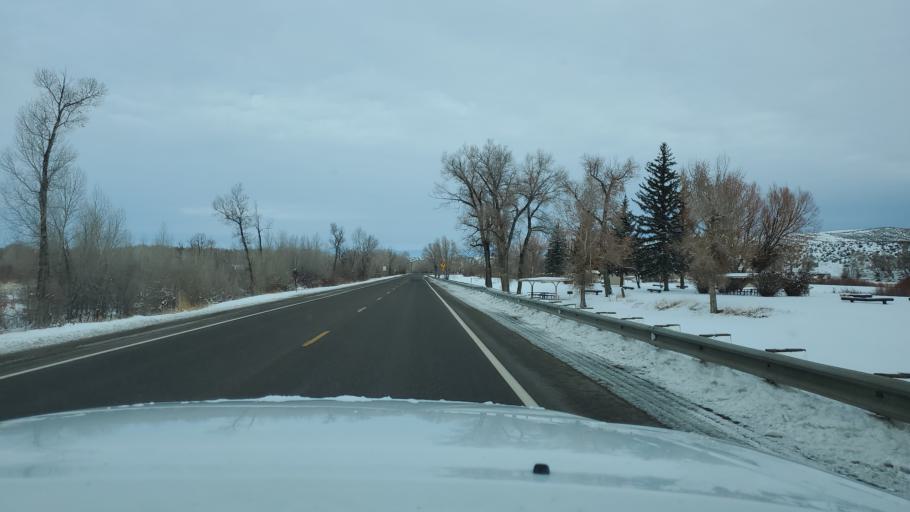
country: US
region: Colorado
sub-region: Routt County
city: Hayden
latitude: 40.4983
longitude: -107.3740
